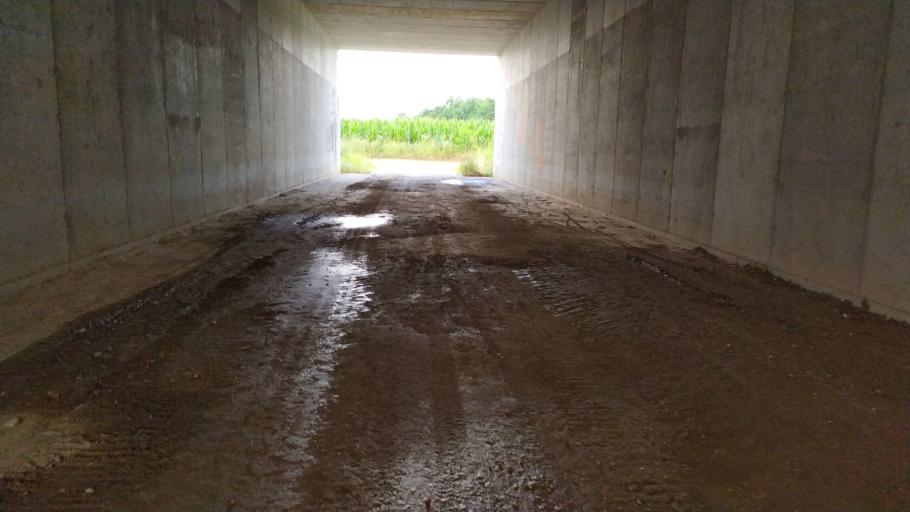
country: IT
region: Veneto
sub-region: Provincia di Vicenza
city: Villaverla
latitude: 45.6512
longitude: 11.4641
